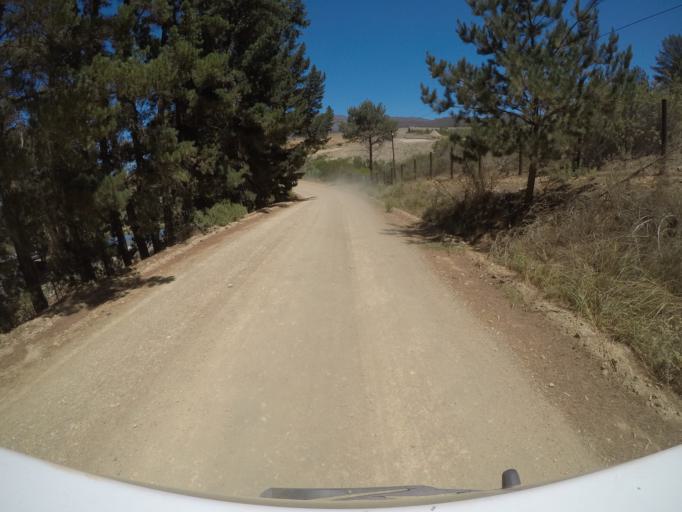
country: ZA
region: Western Cape
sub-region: Overberg District Municipality
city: Caledon
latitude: -34.1747
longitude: 19.2266
